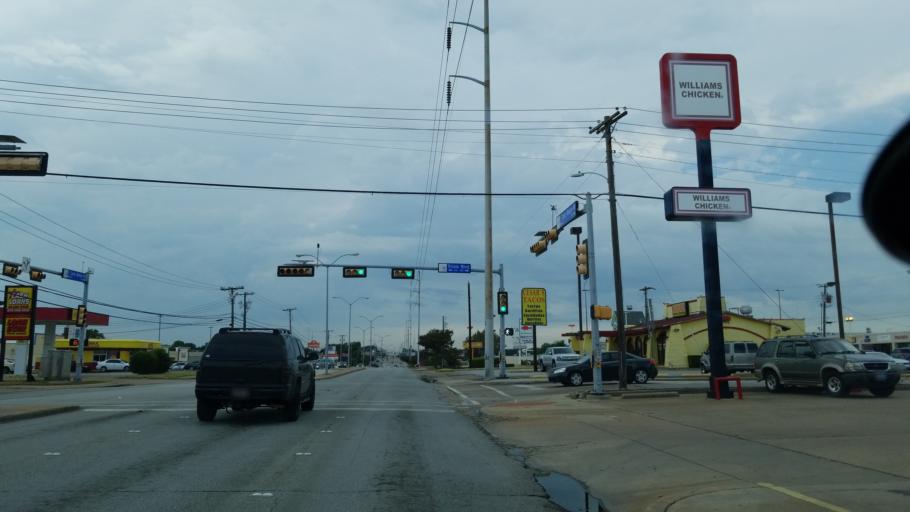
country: US
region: Texas
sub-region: Dallas County
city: Duncanville
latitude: 32.6620
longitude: -96.9005
